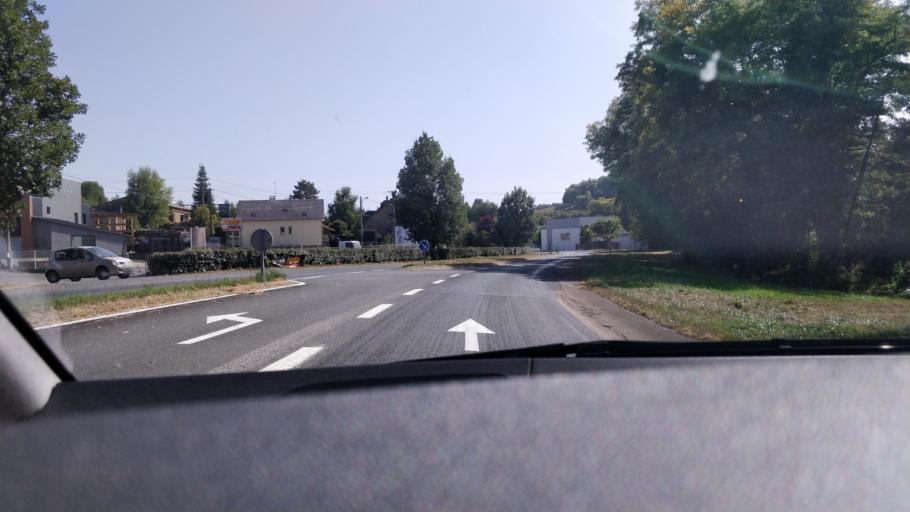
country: FR
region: Limousin
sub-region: Departement de la Correze
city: Uzerche
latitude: 45.4430
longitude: 1.5605
